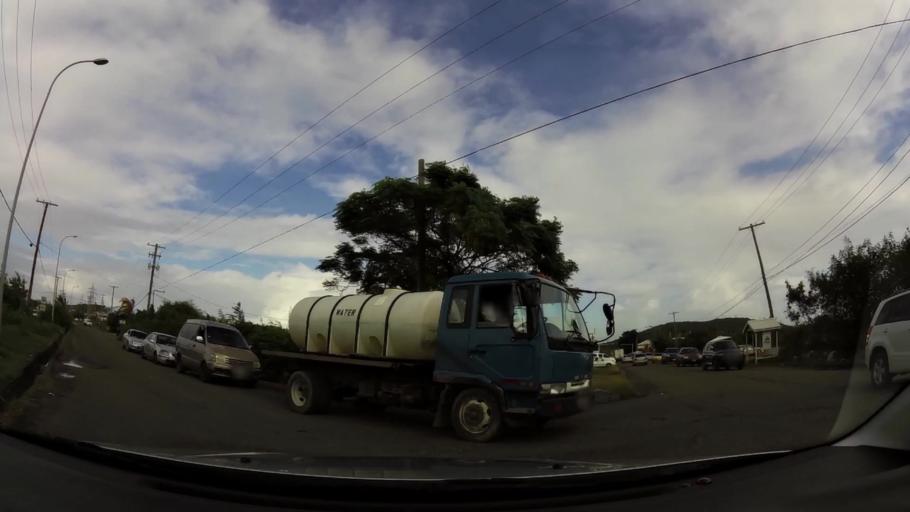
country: AG
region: Saint George
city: Piggotts
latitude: 17.1260
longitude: -61.8144
